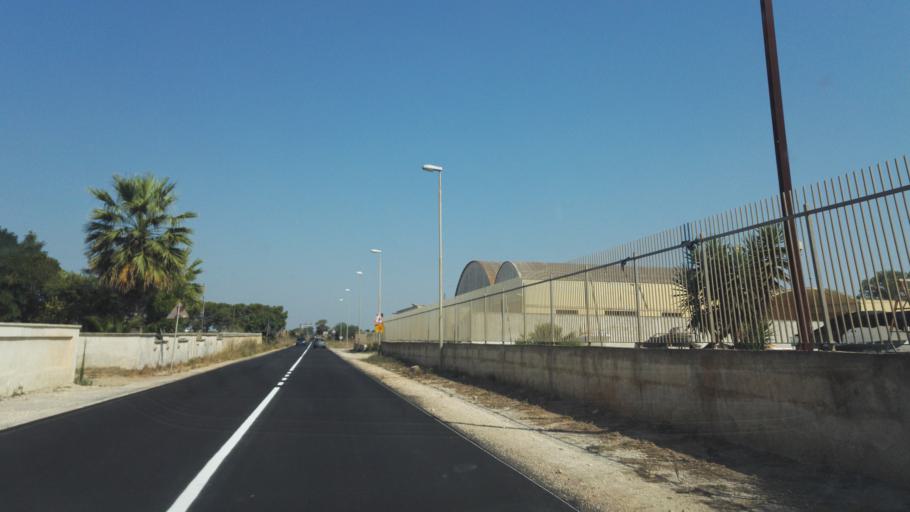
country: IT
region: Apulia
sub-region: Provincia di Lecce
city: Nardo
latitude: 40.2027
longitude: 17.9571
